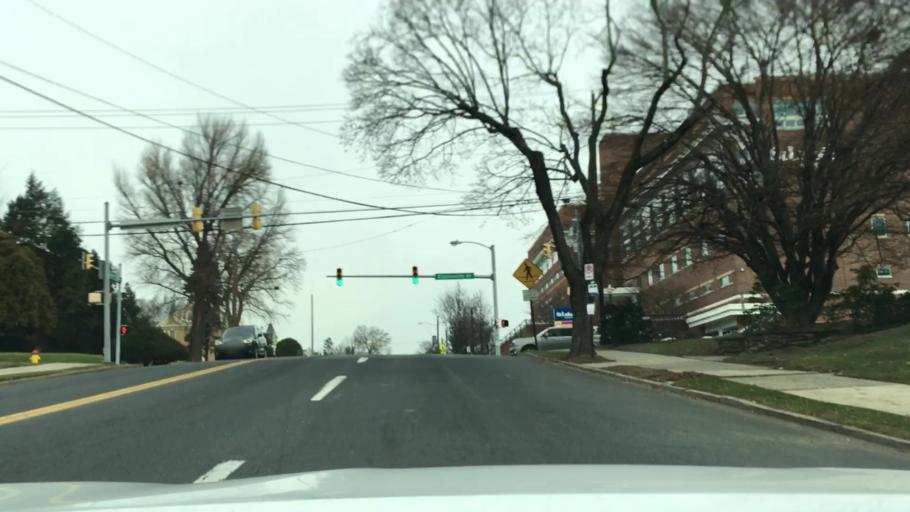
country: US
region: Pennsylvania
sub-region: Lehigh County
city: Allentown
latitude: 40.5958
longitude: -75.4948
